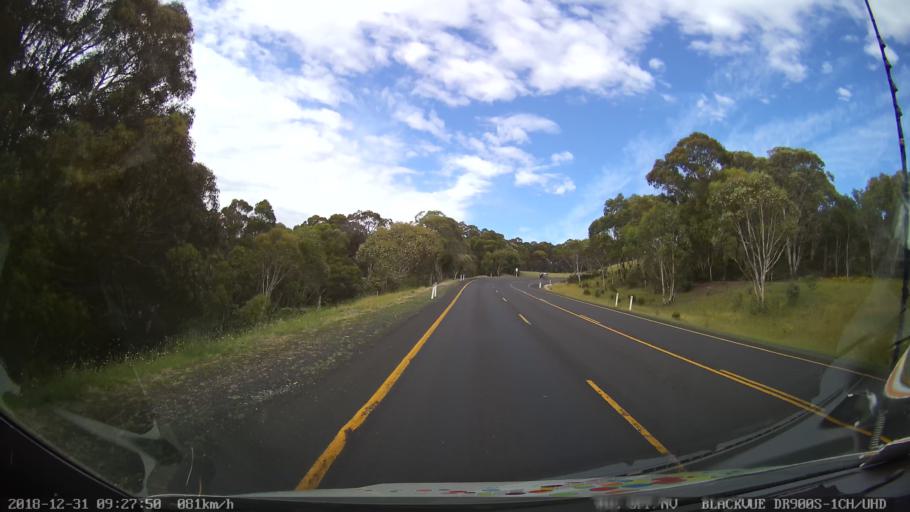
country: AU
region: New South Wales
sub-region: Snowy River
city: Jindabyne
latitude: -36.4590
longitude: 148.4798
